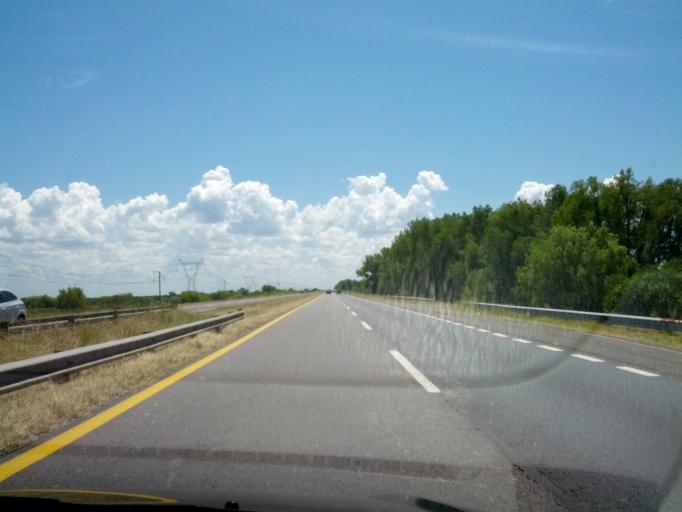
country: AR
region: Entre Rios
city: Villa Paranacito
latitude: -33.7004
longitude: -58.8465
